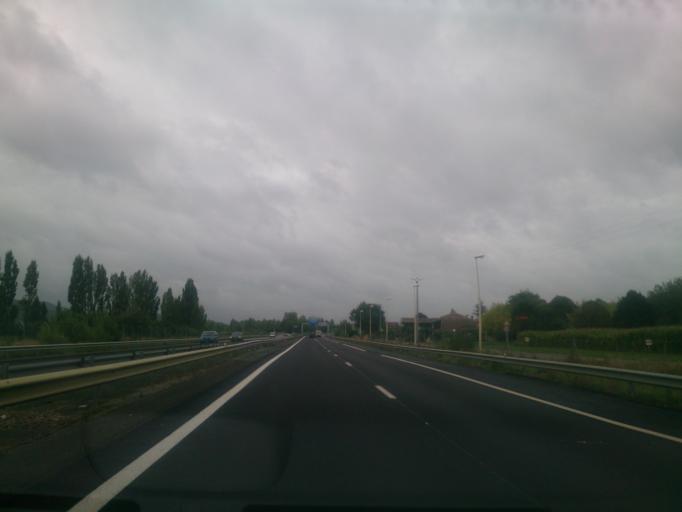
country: FR
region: Midi-Pyrenees
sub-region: Departement de la Haute-Garonne
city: Martres-Tolosane
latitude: 43.2119
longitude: 1.0324
